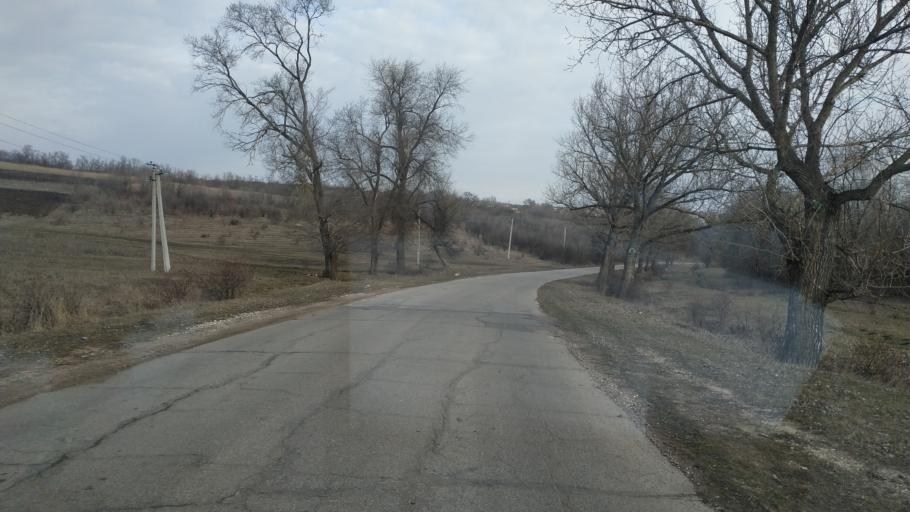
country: MD
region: Chisinau
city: Vadul lui Voda
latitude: 47.0044
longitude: 29.1122
